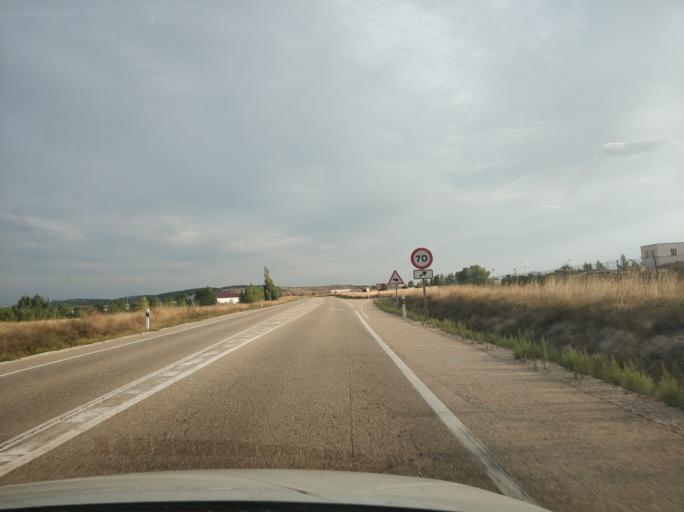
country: ES
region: Castille and Leon
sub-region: Provincia de Burgos
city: Hontoria de la Cantera
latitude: 42.2045
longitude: -3.6490
